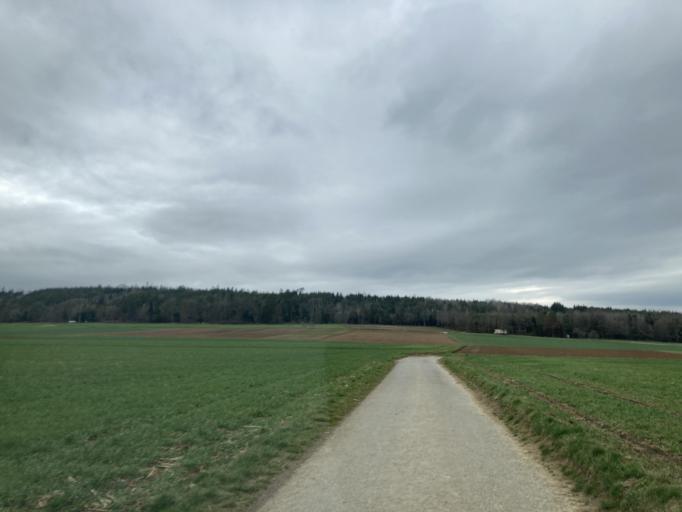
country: DE
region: Baden-Wuerttemberg
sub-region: Regierungsbezirk Stuttgart
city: Bondorf
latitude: 48.4794
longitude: 8.8685
